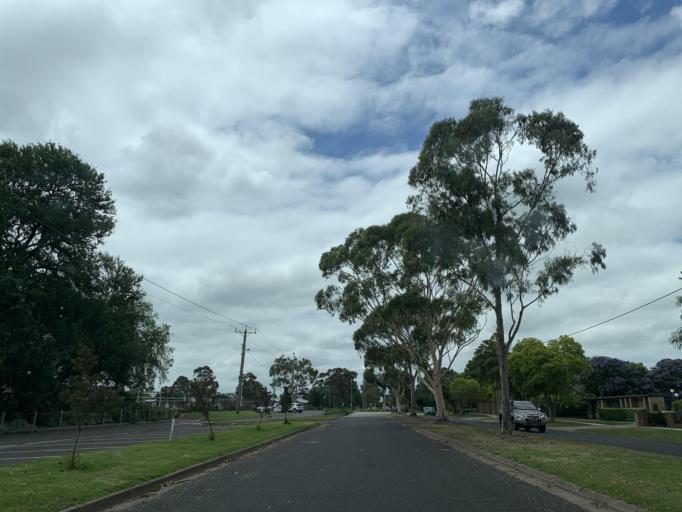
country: AU
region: Victoria
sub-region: Wellington
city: Sale
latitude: -38.1130
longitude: 147.0809
